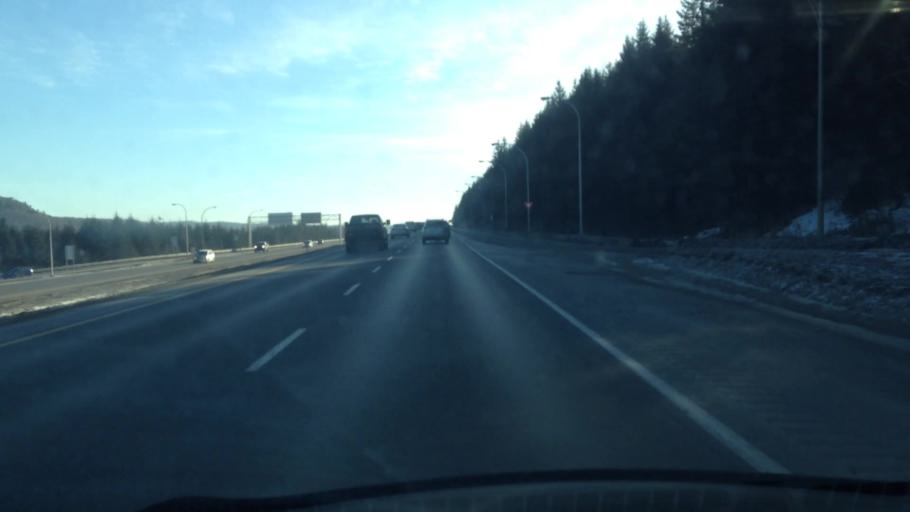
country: CA
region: Quebec
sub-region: Laurentides
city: Prevost
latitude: 45.8831
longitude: -74.1049
